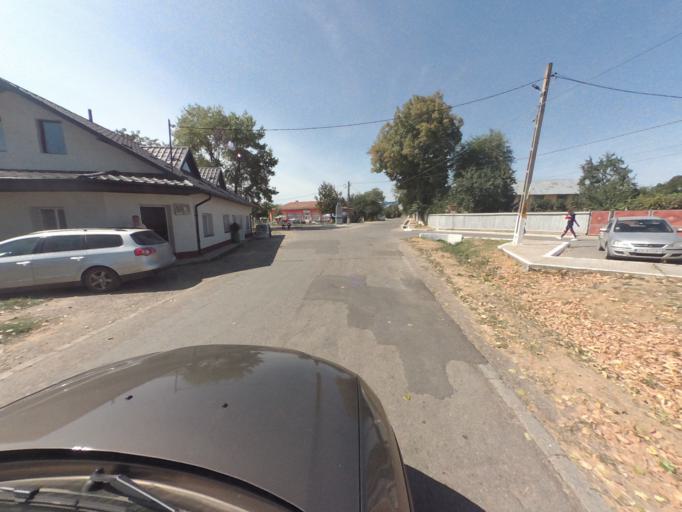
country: RO
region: Vaslui
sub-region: Comuna Deleni
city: Deleni
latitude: 46.5432
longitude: 27.7478
